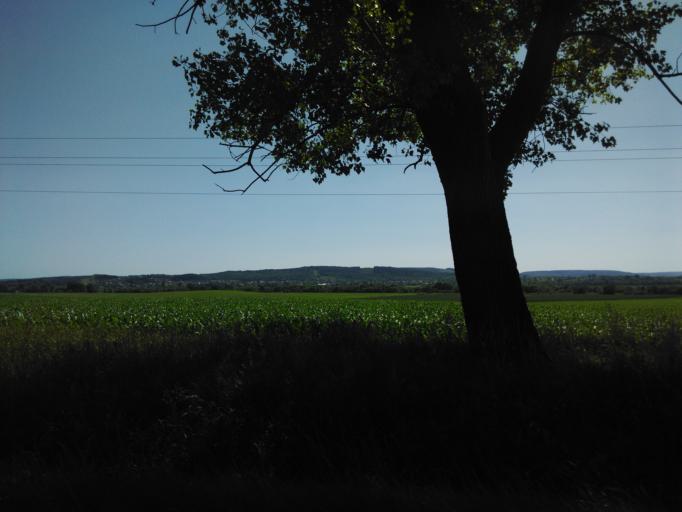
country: HU
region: Fejer
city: Bodajk
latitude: 47.3427
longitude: 18.2377
